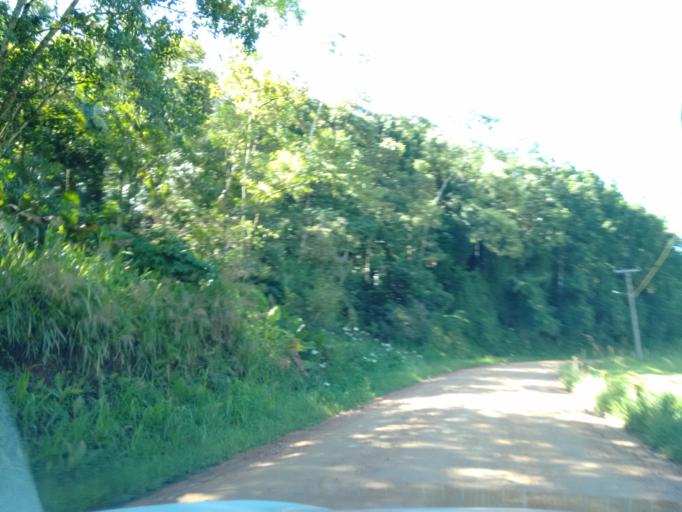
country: BR
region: Santa Catarina
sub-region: Pomerode
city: Pomerode
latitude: -26.7638
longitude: -49.1823
